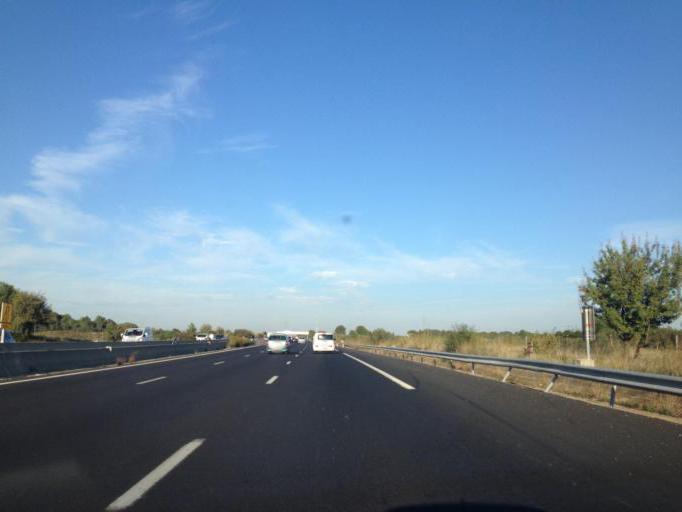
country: FR
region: Languedoc-Roussillon
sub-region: Departement de l'Herault
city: Saint-Bres
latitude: 43.6811
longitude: 4.0418
